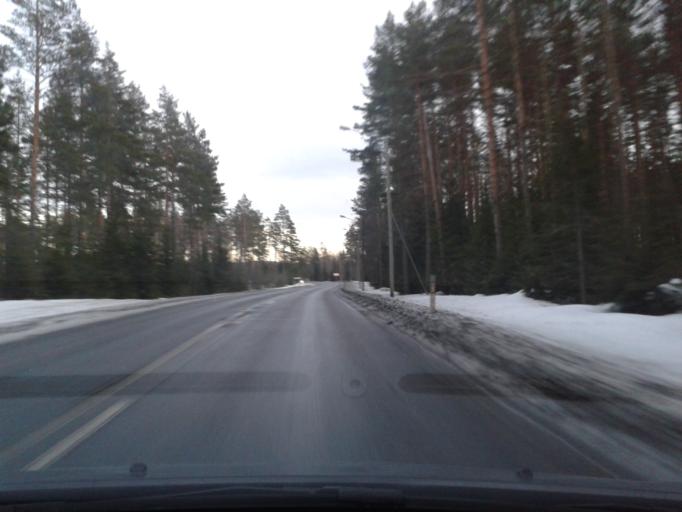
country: SE
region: Vaesternorrland
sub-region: Solleftea Kommun
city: Solleftea
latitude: 63.1544
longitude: 17.3288
